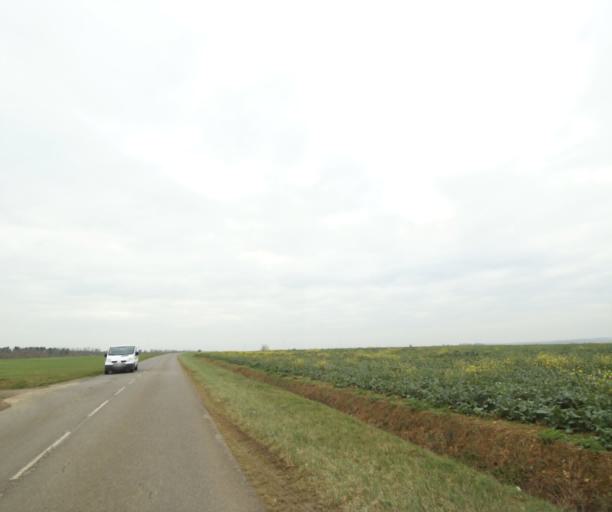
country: FR
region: Lorraine
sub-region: Departement de Meurthe-et-Moselle
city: Mancieulles
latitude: 49.2945
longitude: 5.9079
